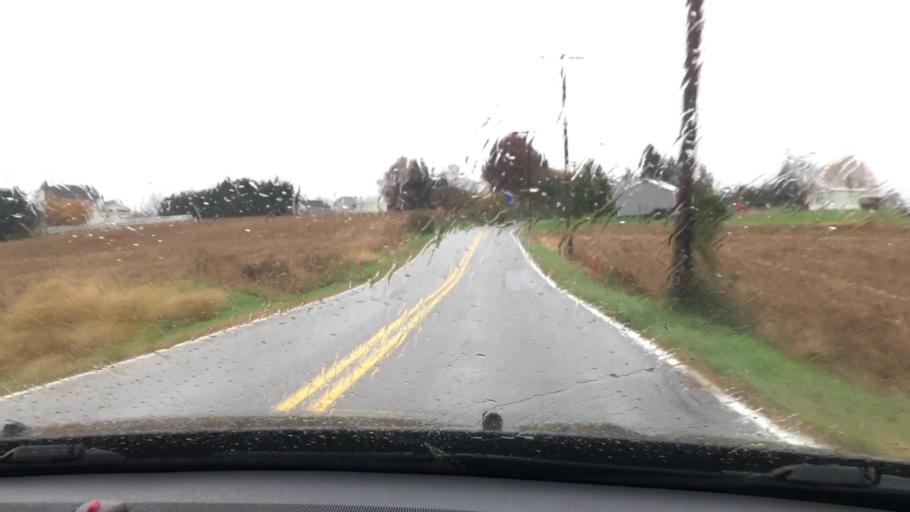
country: US
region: Pennsylvania
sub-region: York County
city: Stewartstown
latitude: 39.7364
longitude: -76.5005
